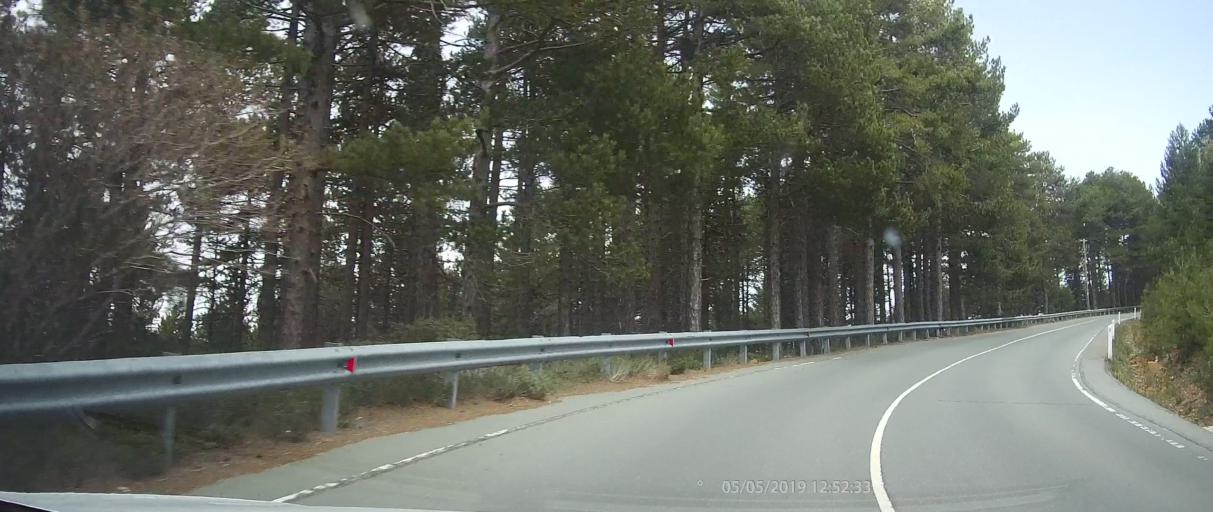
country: CY
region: Lefkosia
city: Kakopetria
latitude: 34.9516
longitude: 32.8370
